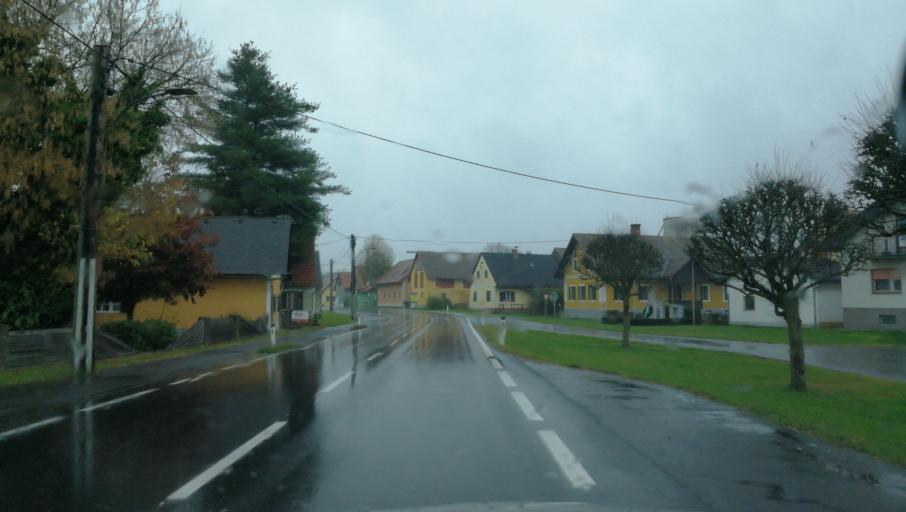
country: SI
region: Sentilj
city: Selnica ob Muri
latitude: 46.7113
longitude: 15.6969
